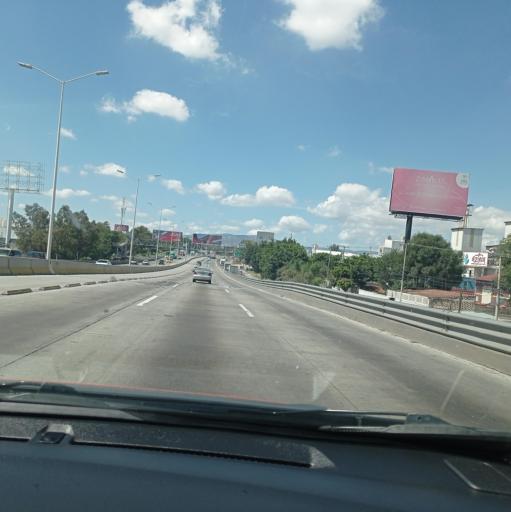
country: MX
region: Jalisco
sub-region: Tlajomulco de Zuniga
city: Altus Bosques
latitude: 20.5768
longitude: -103.3553
